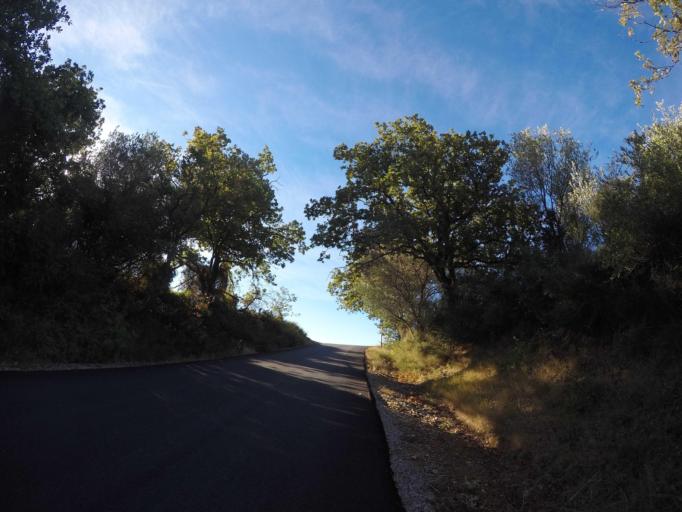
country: FR
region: Languedoc-Roussillon
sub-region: Departement des Pyrenees-Orientales
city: Llupia
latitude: 42.5985
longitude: 2.7653
